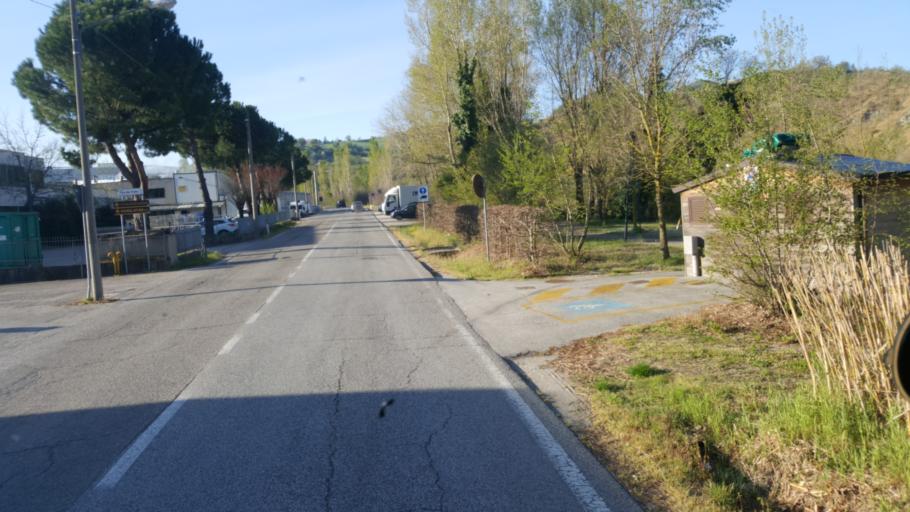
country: SM
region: Acquaviva
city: Acquaviva
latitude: 43.9451
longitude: 12.4055
